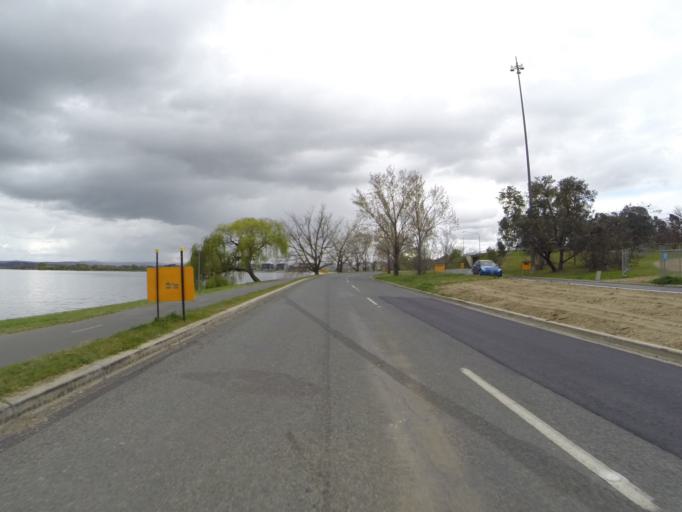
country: AU
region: Australian Capital Territory
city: Forrest
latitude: -35.3025
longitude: 149.1399
